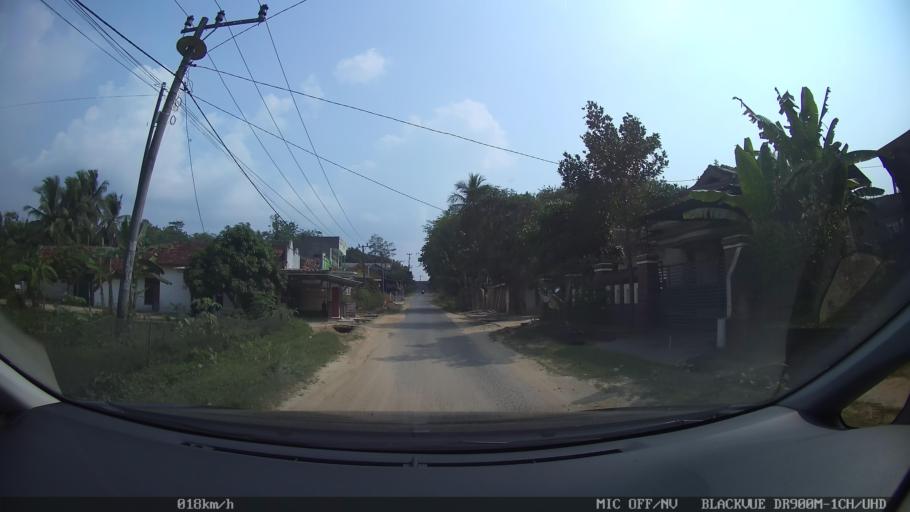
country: ID
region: Lampung
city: Pringsewu
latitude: -5.4029
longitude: 104.9931
